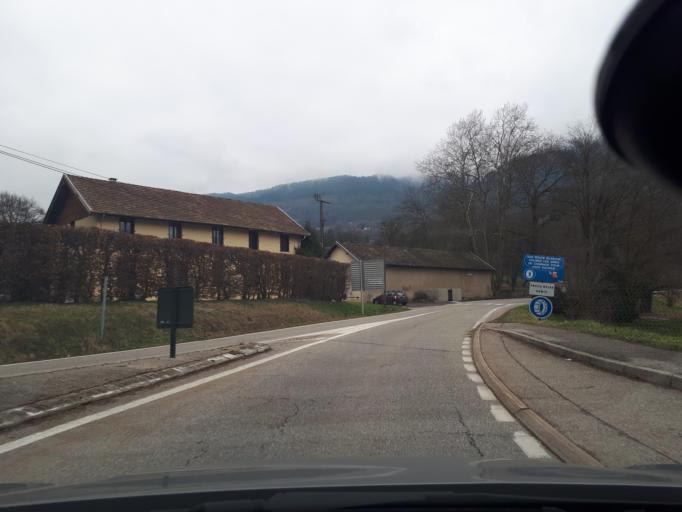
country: FR
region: Rhone-Alpes
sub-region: Departement de l'Isere
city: Vaulnaveys-le-Haut
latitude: 45.1309
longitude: 5.8191
